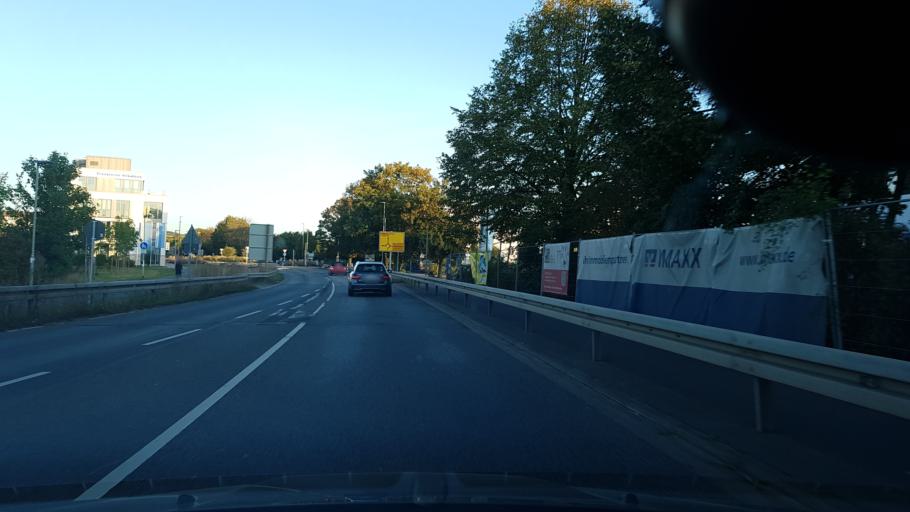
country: DE
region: Hesse
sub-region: Regierungsbezirk Darmstadt
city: Karben
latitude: 50.2346
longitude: 8.7557
